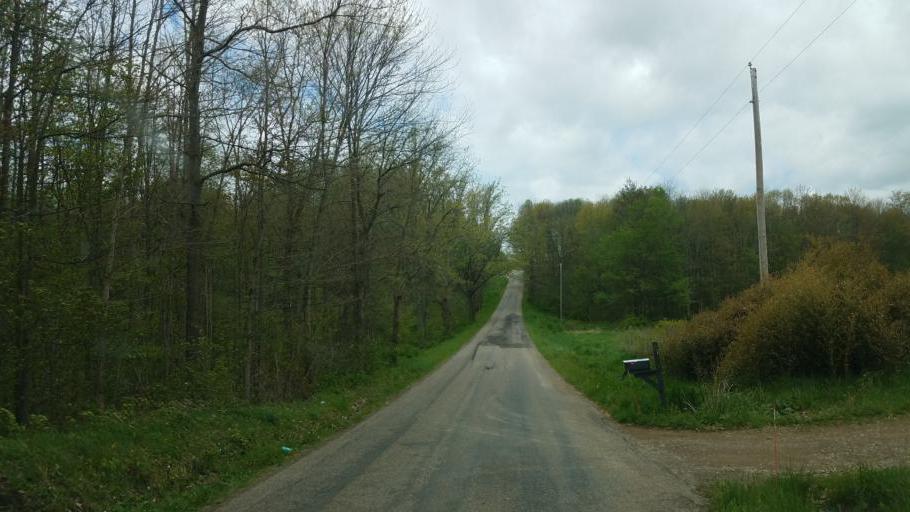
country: US
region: Ohio
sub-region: Ashland County
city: Loudonville
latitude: 40.5724
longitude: -82.3541
